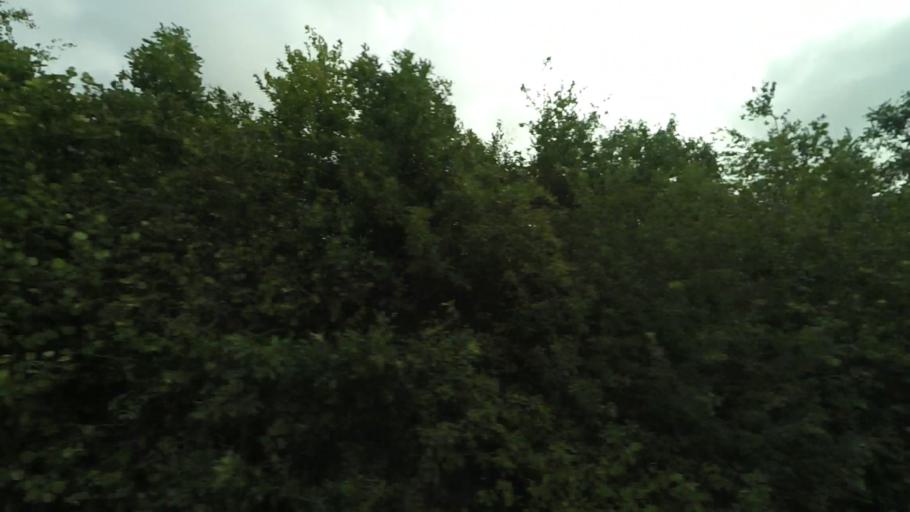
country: DK
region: Central Jutland
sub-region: Syddjurs Kommune
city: Ryomgard
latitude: 56.4363
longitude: 10.5619
